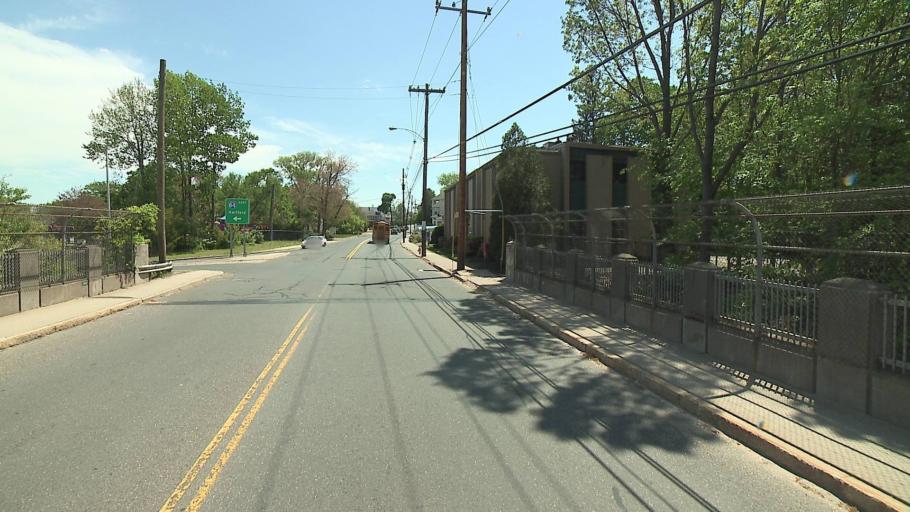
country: US
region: Connecticut
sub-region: New Haven County
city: Waterbury
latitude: 41.5502
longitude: -73.0582
